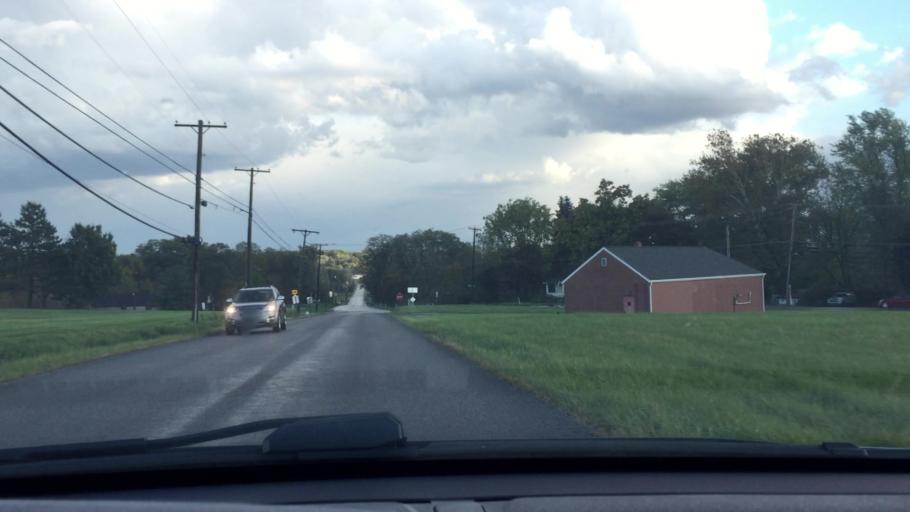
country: US
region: Pennsylvania
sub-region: Lawrence County
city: Bessemer
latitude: 40.9773
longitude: -80.4528
